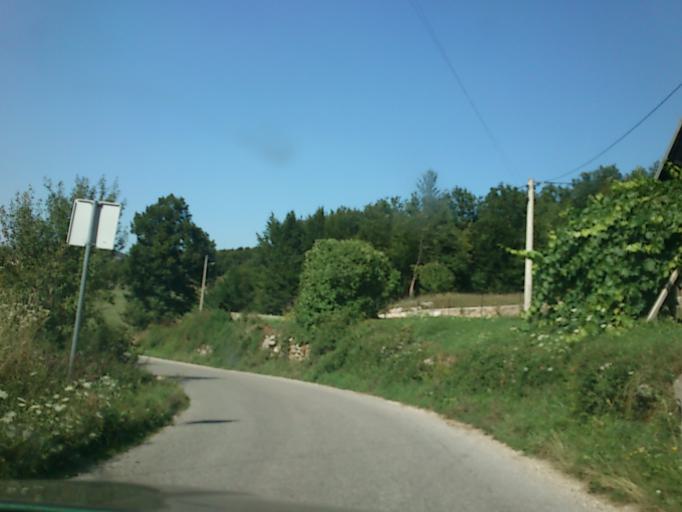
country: HR
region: Licko-Senjska
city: Otocac
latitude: 44.8628
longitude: 15.1723
